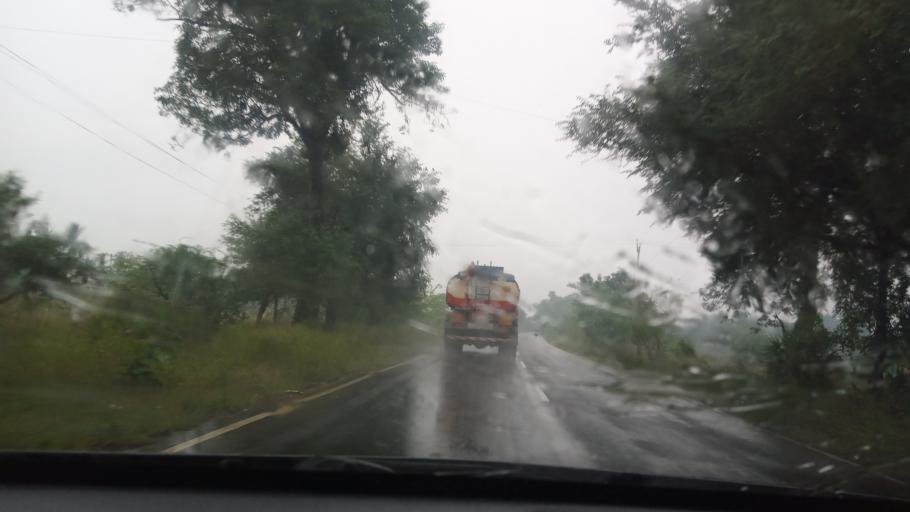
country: IN
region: Tamil Nadu
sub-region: Vellore
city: Kalavai
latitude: 12.8224
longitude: 79.4091
